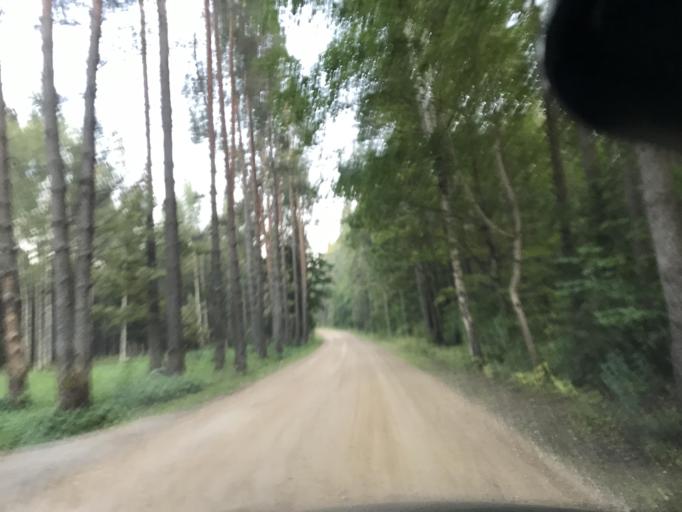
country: LV
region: Ikskile
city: Ikskile
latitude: 56.8286
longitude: 24.5129
